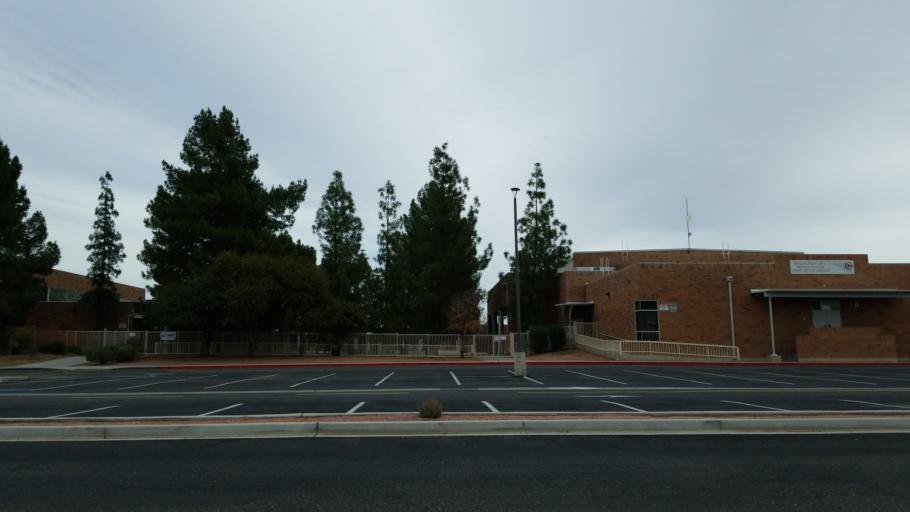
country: US
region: Arizona
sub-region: Maricopa County
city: Glendale
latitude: 33.6319
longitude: -112.0827
